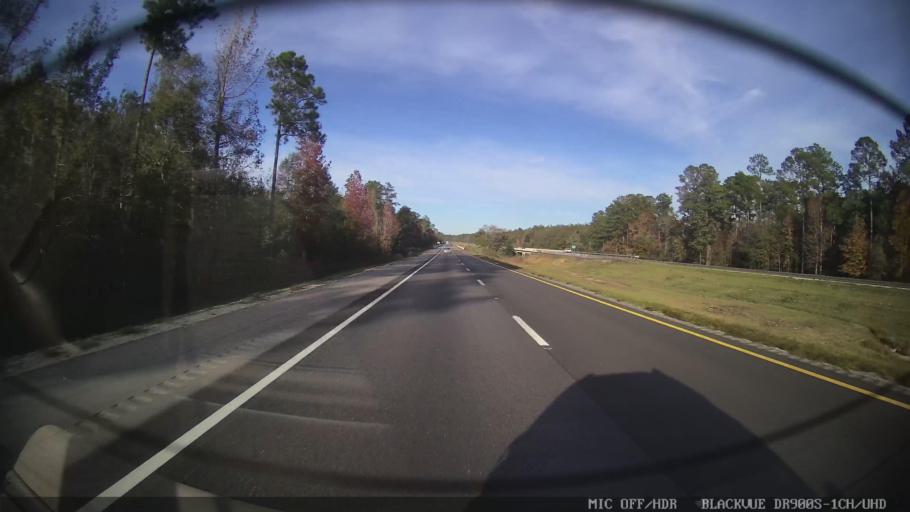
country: US
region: Mississippi
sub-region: Lamar County
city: Purvis
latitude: 31.1673
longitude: -89.3534
